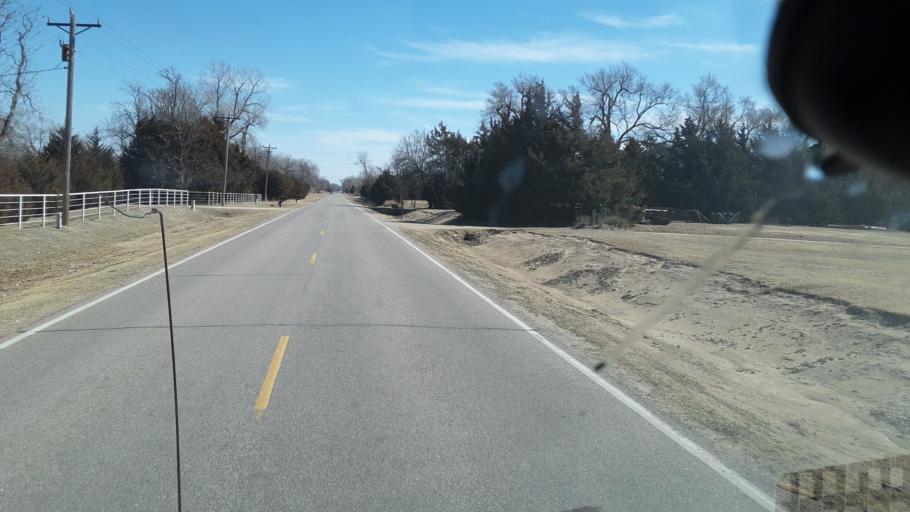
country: US
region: Kansas
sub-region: Reno County
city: Hutchinson
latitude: 38.1593
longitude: -97.9129
